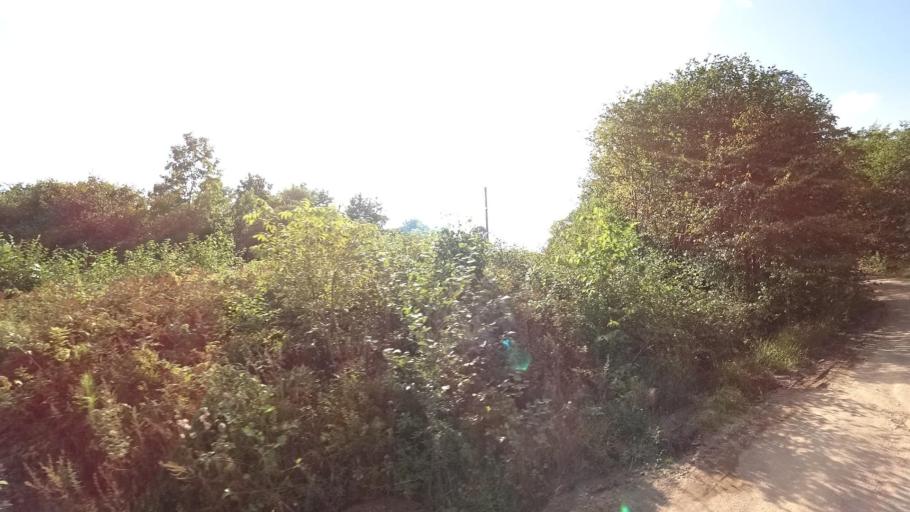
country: RU
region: Jewish Autonomous Oblast
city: Birakan
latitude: 49.0022
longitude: 131.7123
